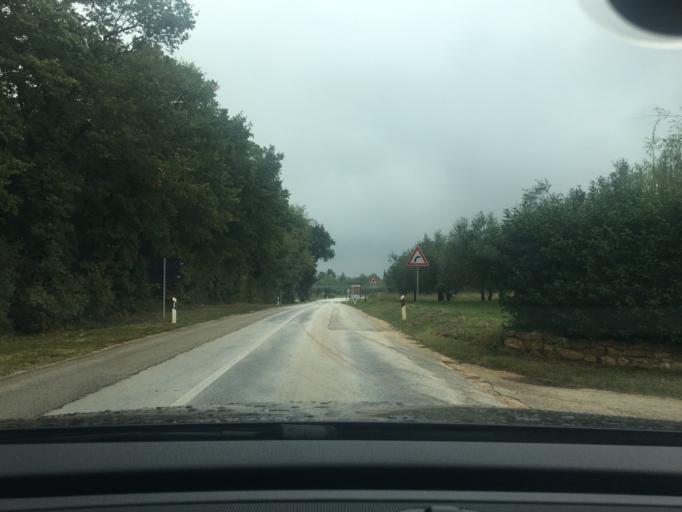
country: HR
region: Istarska
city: Buje
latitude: 45.3651
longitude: 13.6085
